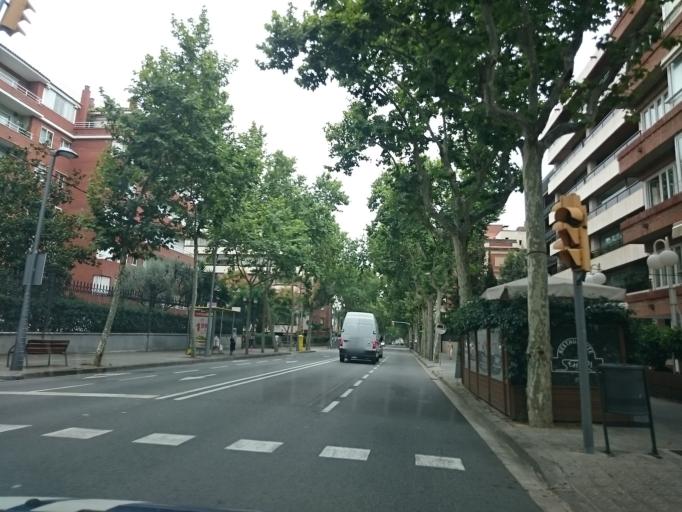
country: ES
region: Catalonia
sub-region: Provincia de Barcelona
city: Sarria-Sant Gervasi
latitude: 41.4051
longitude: 2.1306
